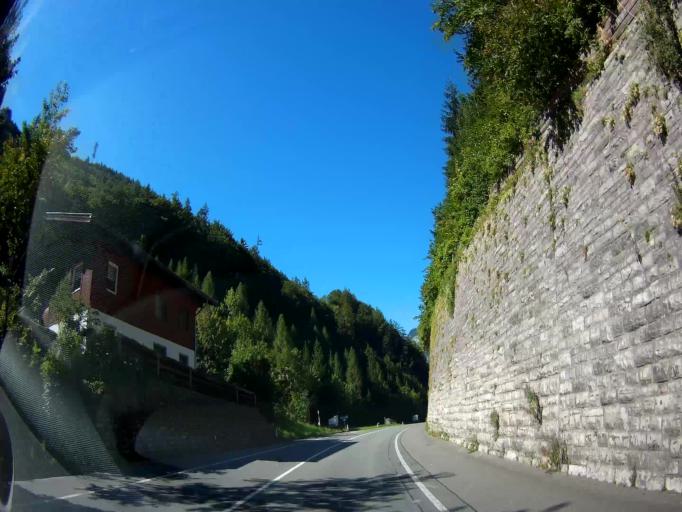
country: AT
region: Salzburg
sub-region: Politischer Bezirk Sankt Johann im Pongau
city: Werfen
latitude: 47.4813
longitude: 13.1851
